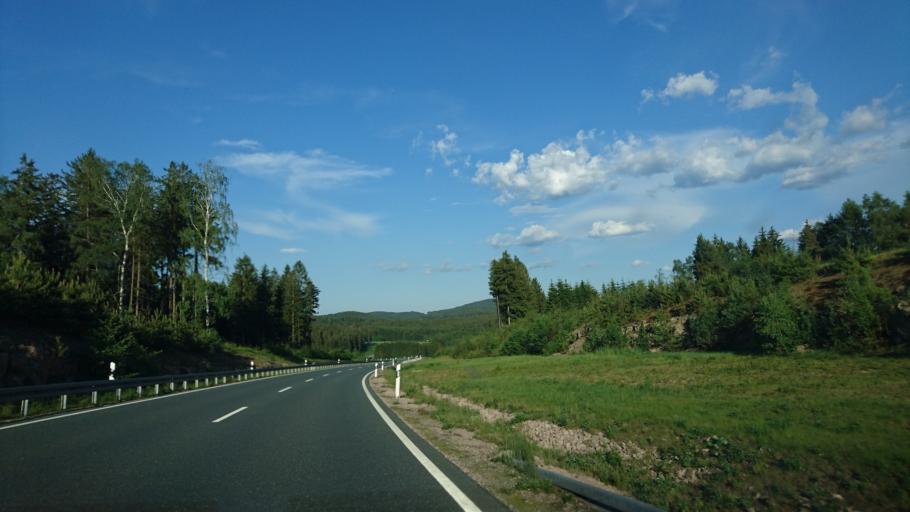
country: DE
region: Saxony
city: Stutzengrun
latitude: 50.5519
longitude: 12.5702
